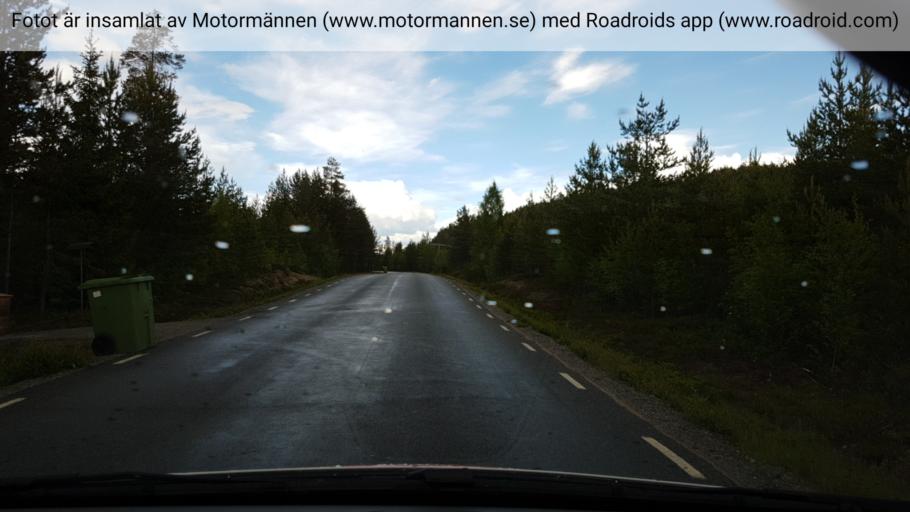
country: SE
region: Vaesterbotten
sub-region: Umea Kommun
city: Roback
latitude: 63.9828
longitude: 20.1207
